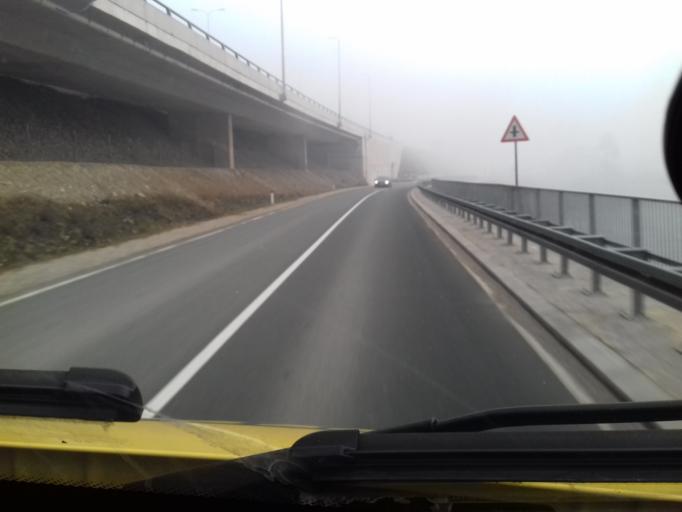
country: BA
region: Federation of Bosnia and Herzegovina
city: Kacuni
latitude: 44.1338
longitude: 17.9911
